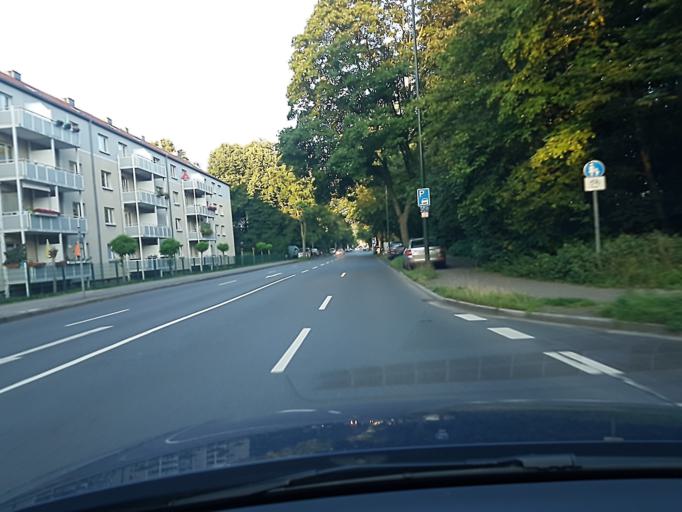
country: DE
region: North Rhine-Westphalia
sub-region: Regierungsbezirk Dusseldorf
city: Dusseldorf
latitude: 51.2427
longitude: 6.8159
